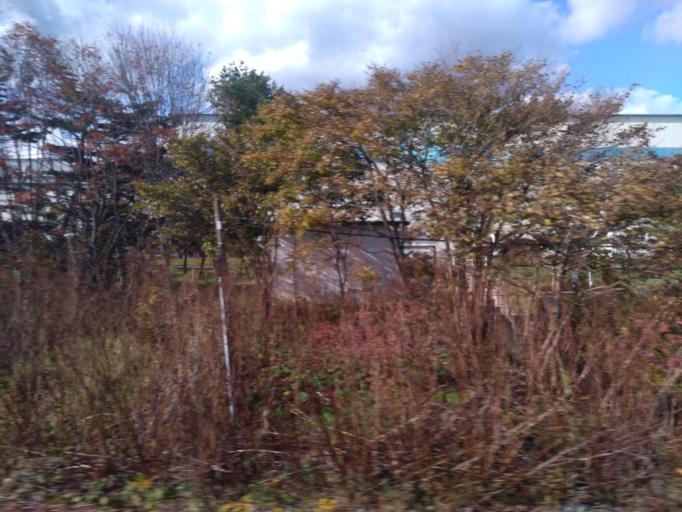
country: JP
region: Hokkaido
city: Shiraoi
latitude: 42.5127
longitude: 141.2920
